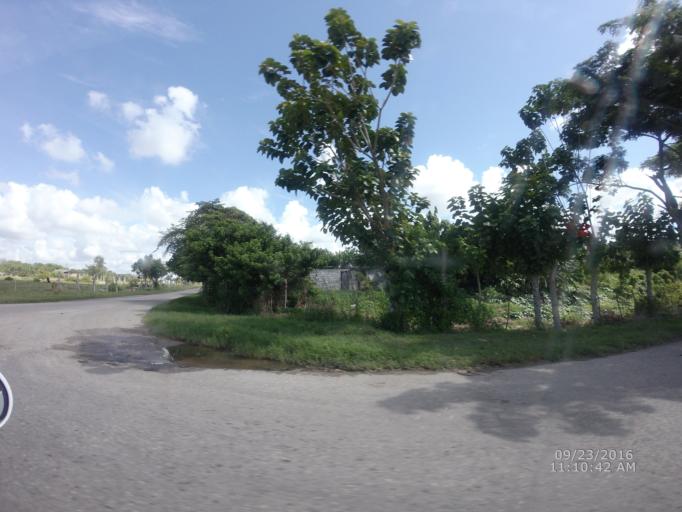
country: CU
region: La Habana
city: Arroyo Naranjo
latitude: 23.0220
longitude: -82.2594
